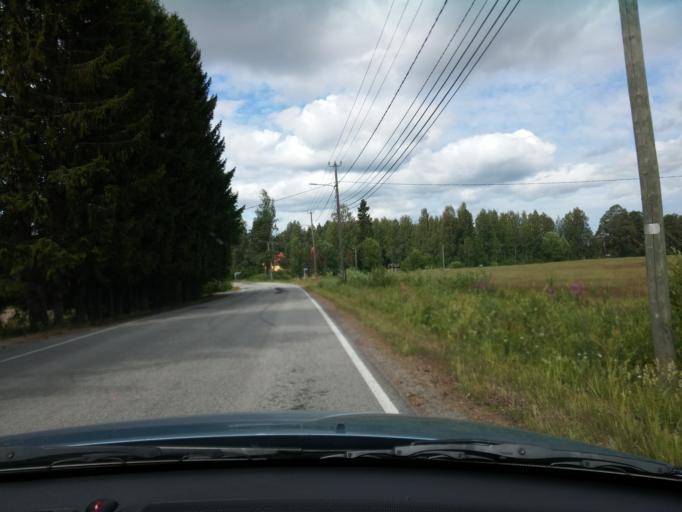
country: FI
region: Central Finland
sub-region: Saarijaervi-Viitasaari
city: Saarijaervi
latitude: 62.7349
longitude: 25.1849
